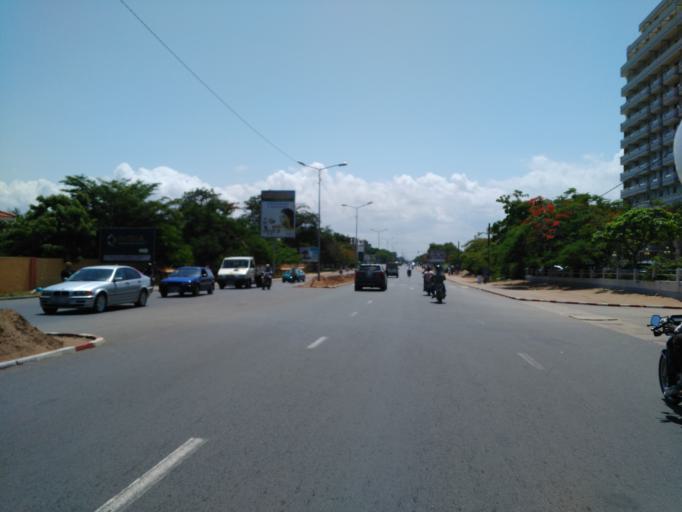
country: TG
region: Maritime
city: Lome
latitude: 6.1534
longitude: 1.2289
